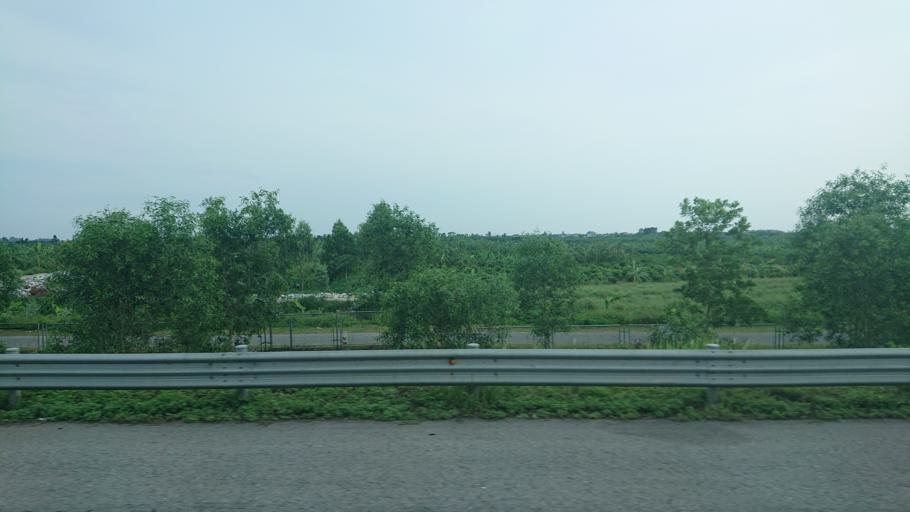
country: VN
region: Hai Duong
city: Tu Ky
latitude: 20.8280
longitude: 106.4558
